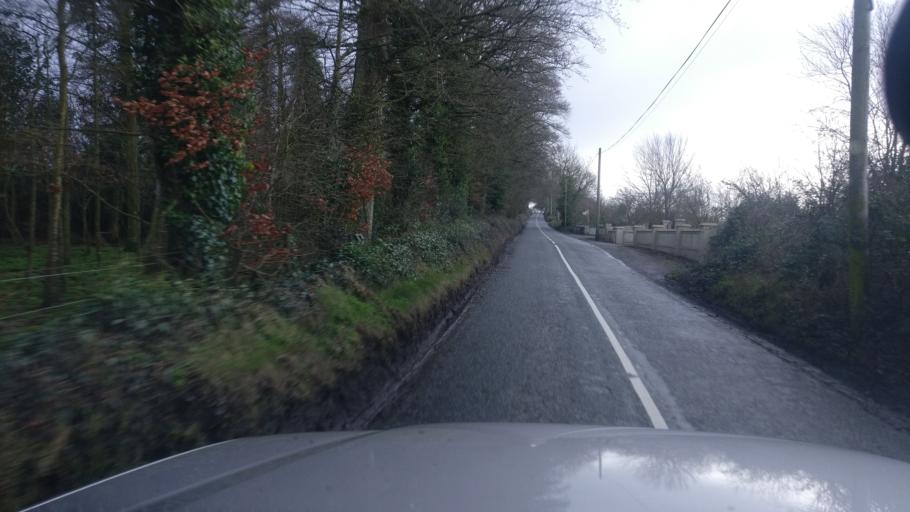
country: IE
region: Munster
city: Nenagh Bridge
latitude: 52.9762
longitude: -8.0924
